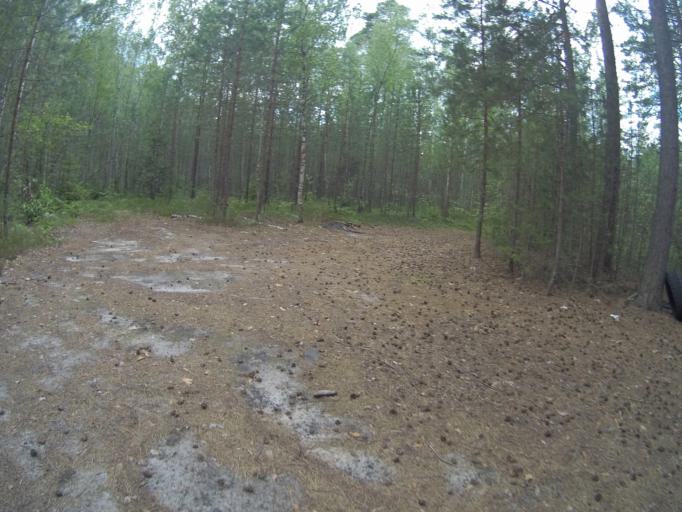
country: RU
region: Vladimir
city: Raduzhnyy
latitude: 56.0589
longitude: 40.3114
